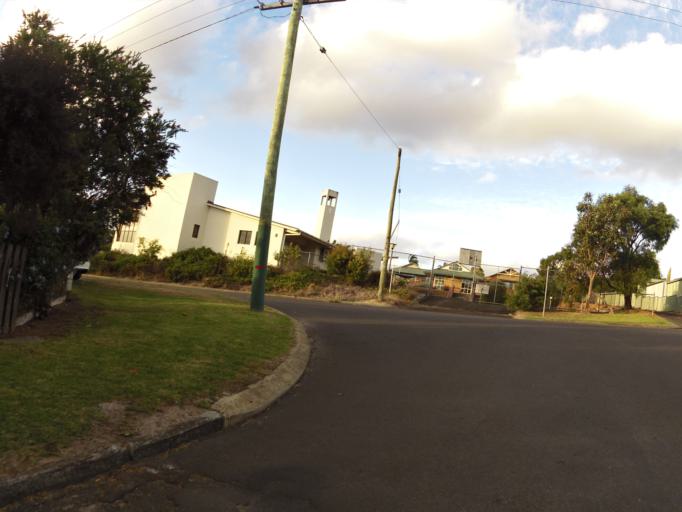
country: AU
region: Western Australia
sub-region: Manjimup
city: Pemberton
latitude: -34.4471
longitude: 116.0343
